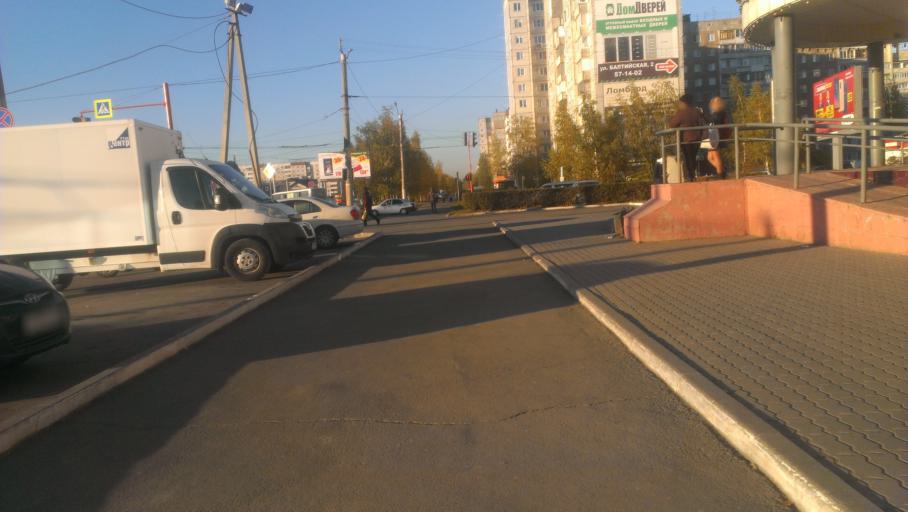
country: RU
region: Altai Krai
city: Novosilikatnyy
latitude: 53.3355
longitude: 83.6695
